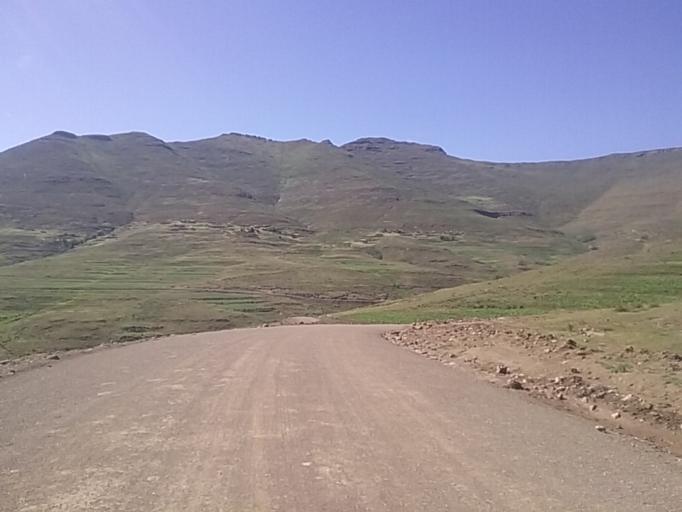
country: LS
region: Qacha's Nek
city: Qacha's Nek
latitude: -30.1690
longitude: 28.2127
